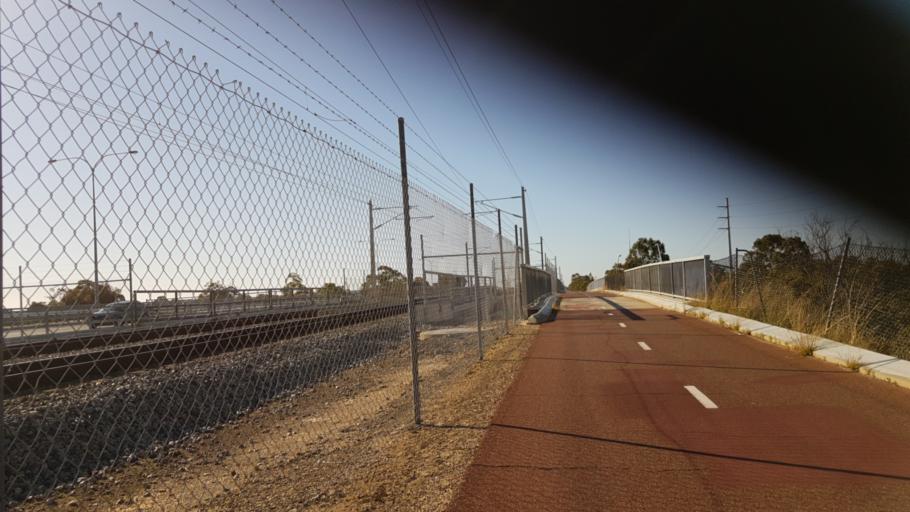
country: AU
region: Western Australia
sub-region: Gosnells
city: Kenwick
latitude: -32.0330
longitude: 115.9661
